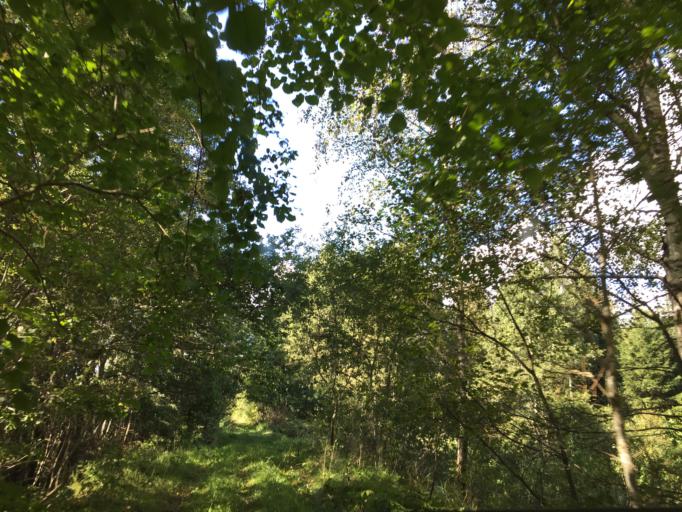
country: LV
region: Kuldigas Rajons
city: Kuldiga
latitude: 56.9779
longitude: 21.9057
